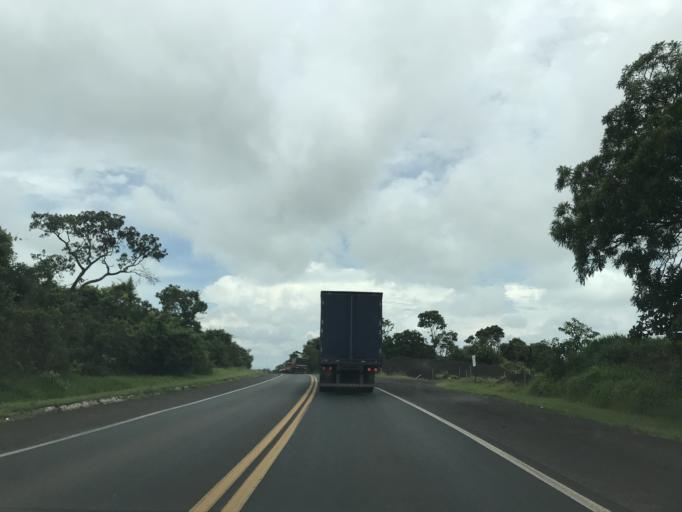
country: BR
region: Minas Gerais
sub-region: Frutal
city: Frutal
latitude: -19.7689
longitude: -48.9648
